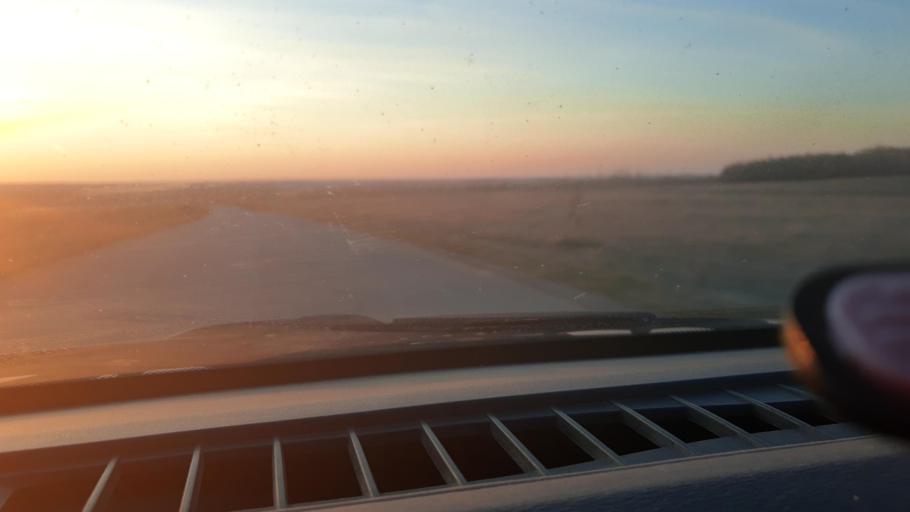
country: RU
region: Bashkortostan
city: Asanovo
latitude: 54.8191
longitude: 55.4757
